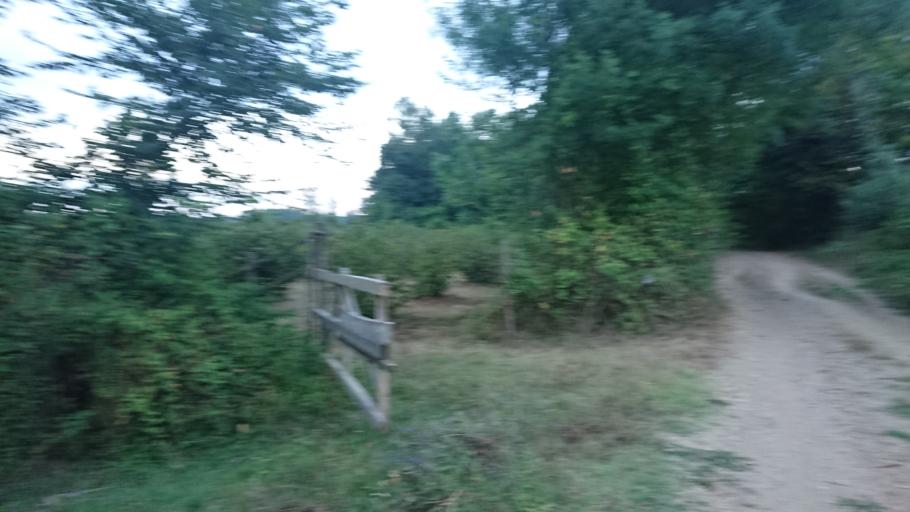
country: TR
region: Samsun
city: Dikbiyik
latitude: 41.1790
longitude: 36.5502
